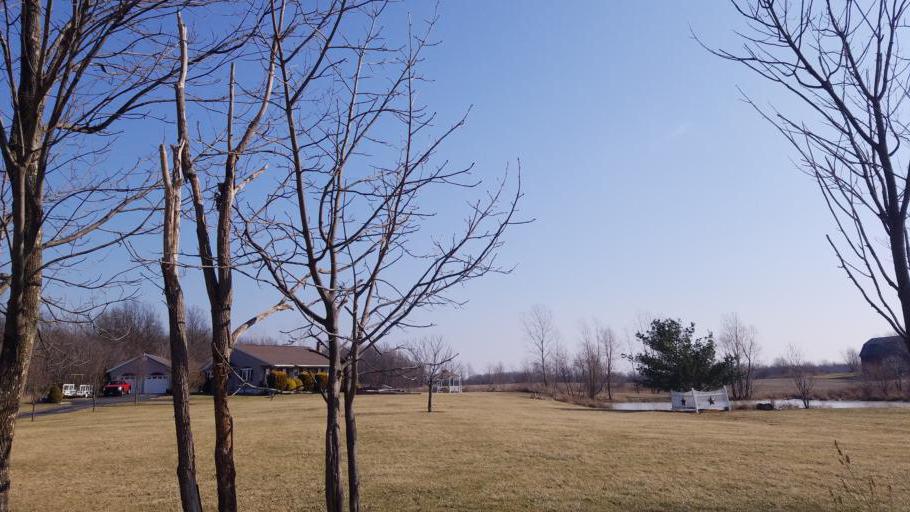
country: US
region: Ohio
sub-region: Richland County
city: Ontario
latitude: 40.8357
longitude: -82.5522
